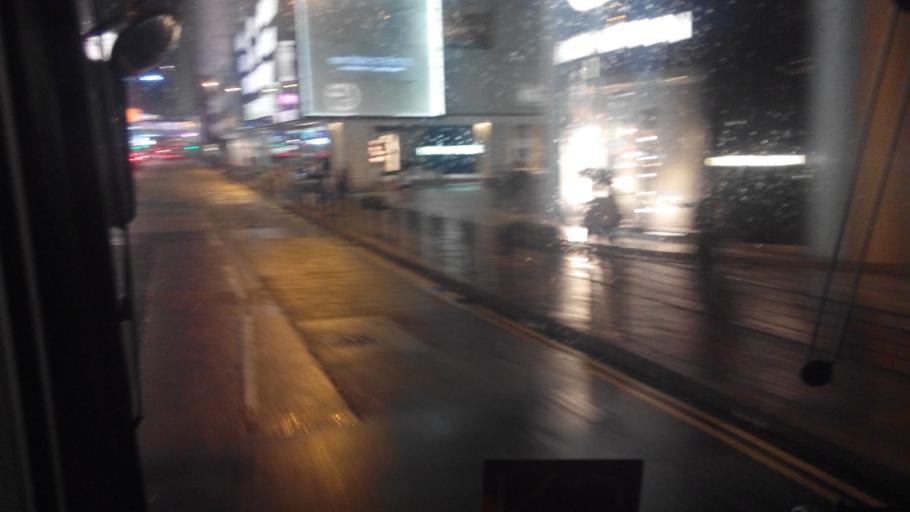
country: HK
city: Hong Kong
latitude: 22.2994
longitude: 114.1681
